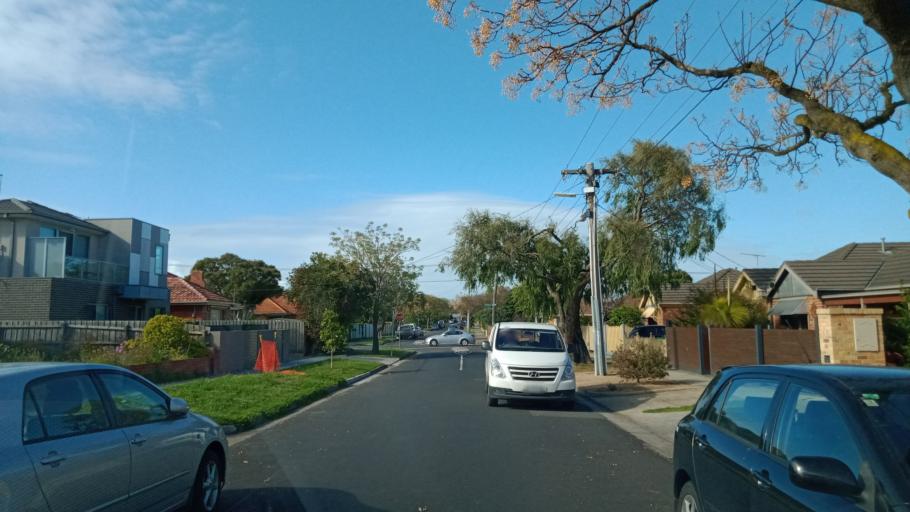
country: AU
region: Victoria
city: McKinnon
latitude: -37.9224
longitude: 145.0560
